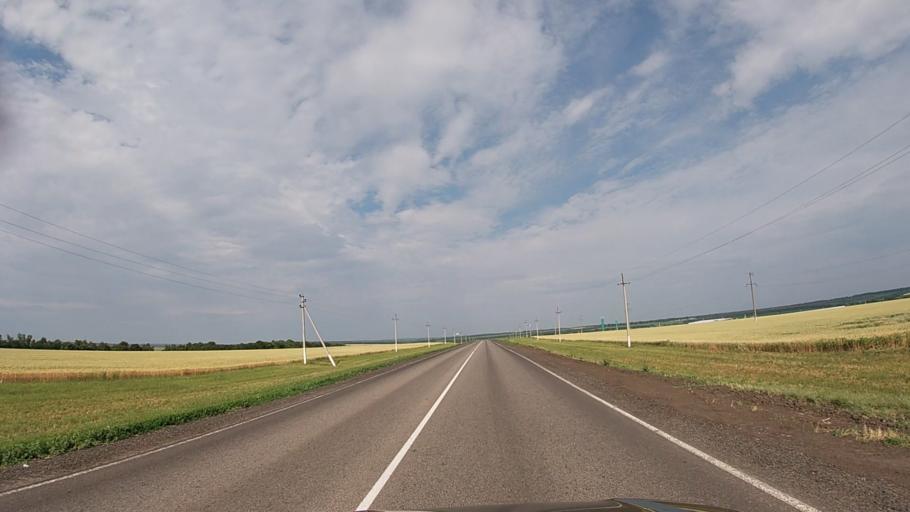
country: RU
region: Belgorod
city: Krasnaya Yaruga
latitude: 50.7980
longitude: 35.5928
